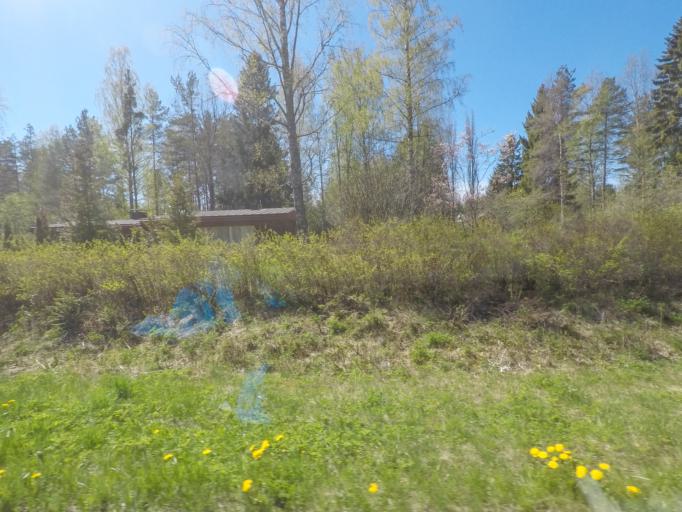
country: FI
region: Uusimaa
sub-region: Helsinki
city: Sammatti
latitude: 60.3250
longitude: 23.8161
